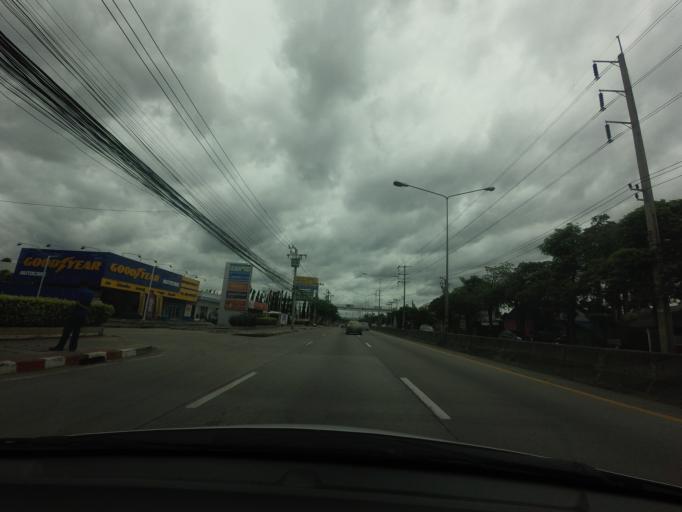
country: TH
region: Bangkok
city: Min Buri
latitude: 13.7909
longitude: 100.7461
